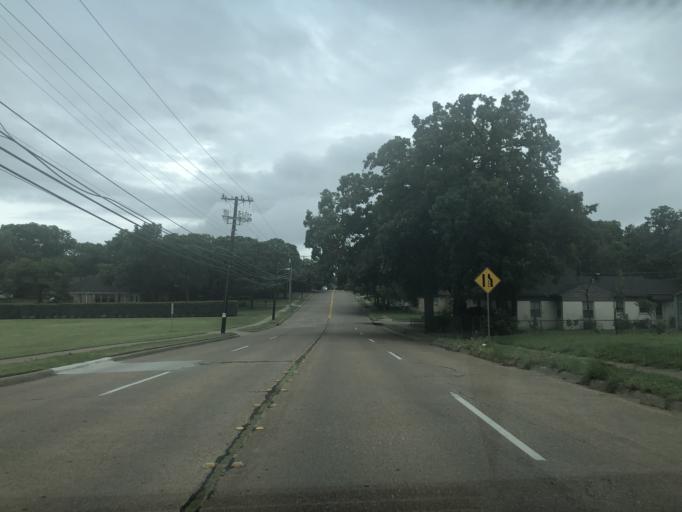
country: US
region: Texas
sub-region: Dallas County
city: Irving
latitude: 32.8005
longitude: -96.9469
